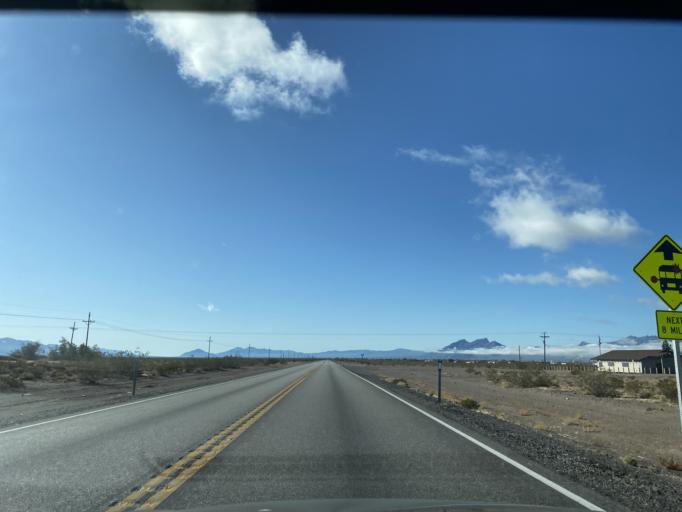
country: US
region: Nevada
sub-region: Nye County
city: Beatty
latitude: 36.5270
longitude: -116.4191
